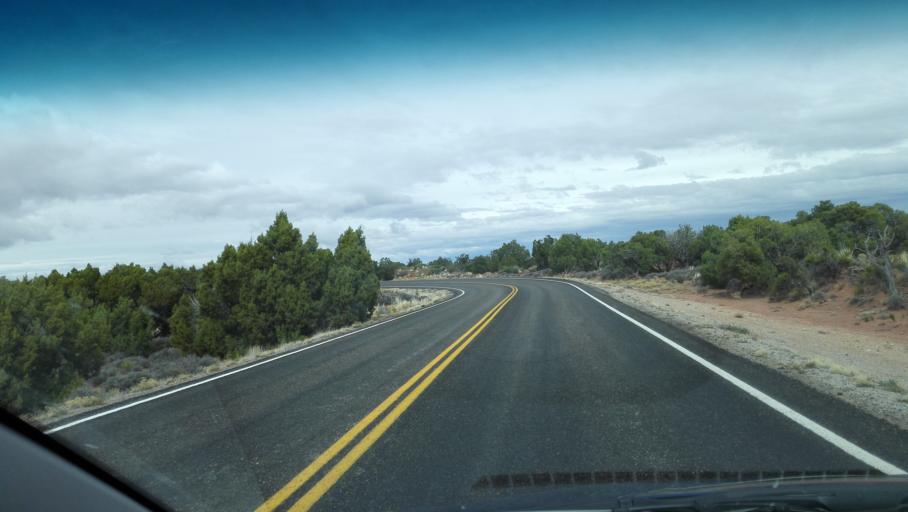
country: US
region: Utah
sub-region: Grand County
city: Moab
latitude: 38.3322
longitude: -109.8542
